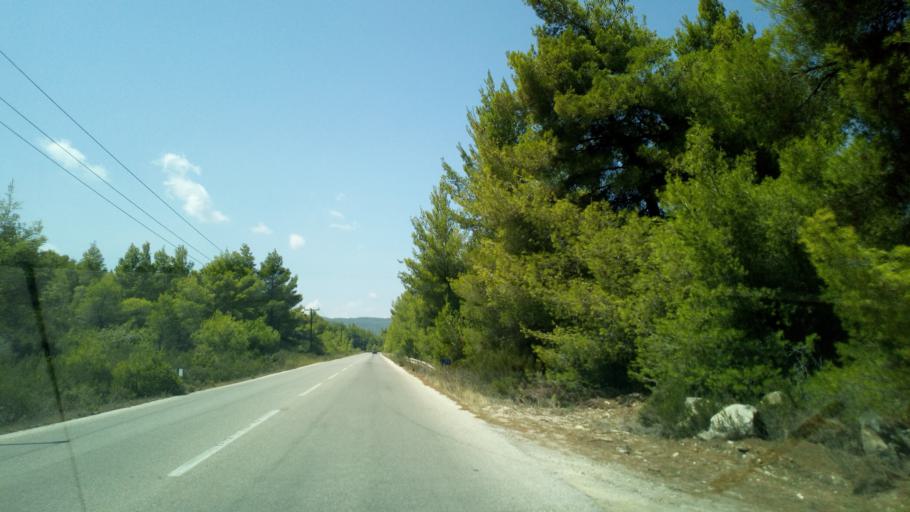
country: GR
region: Central Macedonia
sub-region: Nomos Chalkidikis
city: Sarti
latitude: 40.1251
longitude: 23.9504
